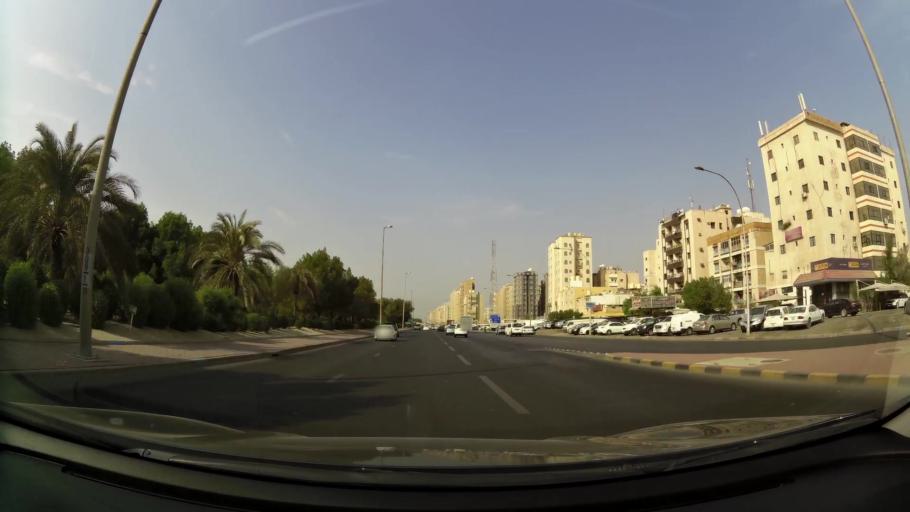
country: KW
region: Al Farwaniyah
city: Al Farwaniyah
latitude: 29.2823
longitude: 47.9682
